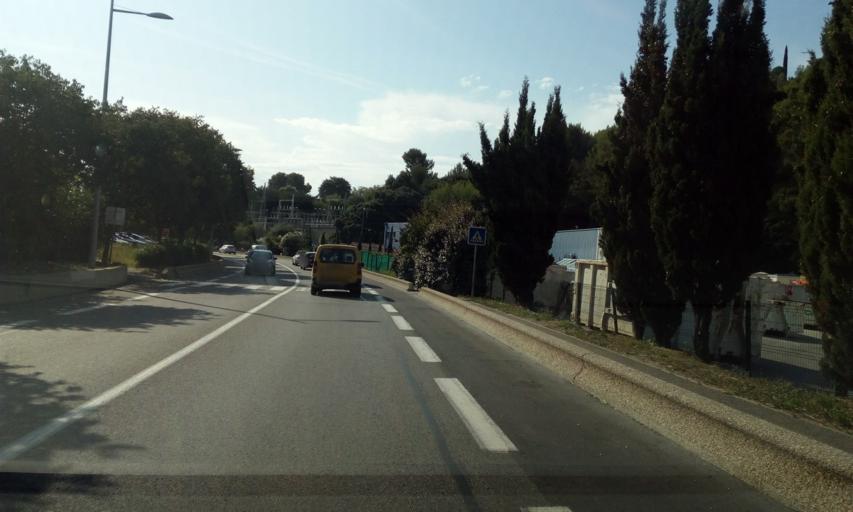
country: FR
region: Provence-Alpes-Cote d'Azur
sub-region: Departement du Var
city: Bandol
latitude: 43.1471
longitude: 5.7651
